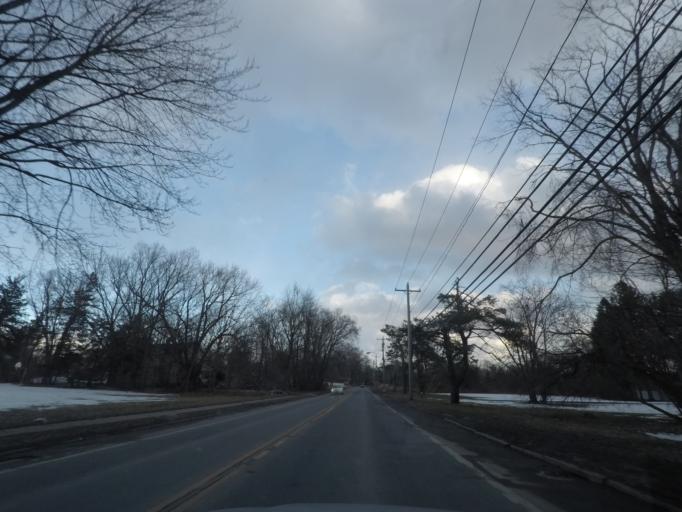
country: US
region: New York
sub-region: Oneida County
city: Utica
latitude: 43.1084
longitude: -75.1715
